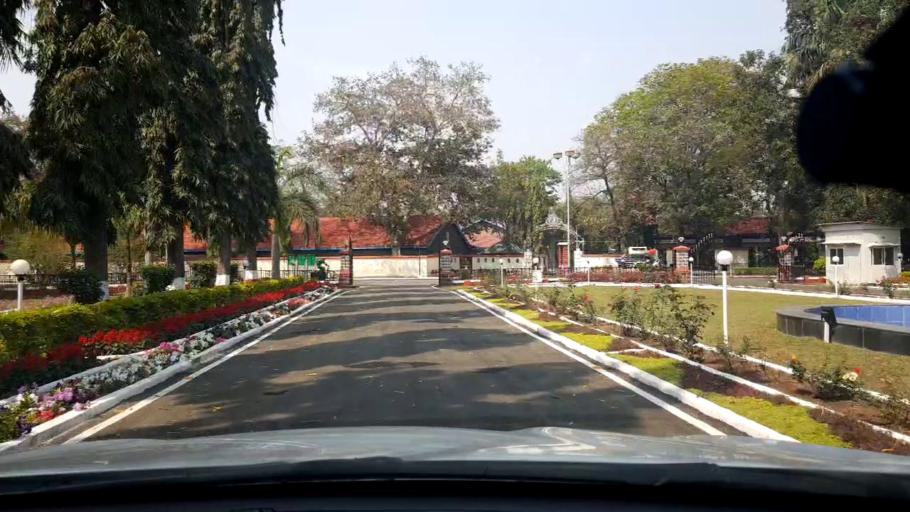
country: IN
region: Maharashtra
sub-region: Pune Division
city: Khadki
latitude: 18.5502
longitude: 73.8634
